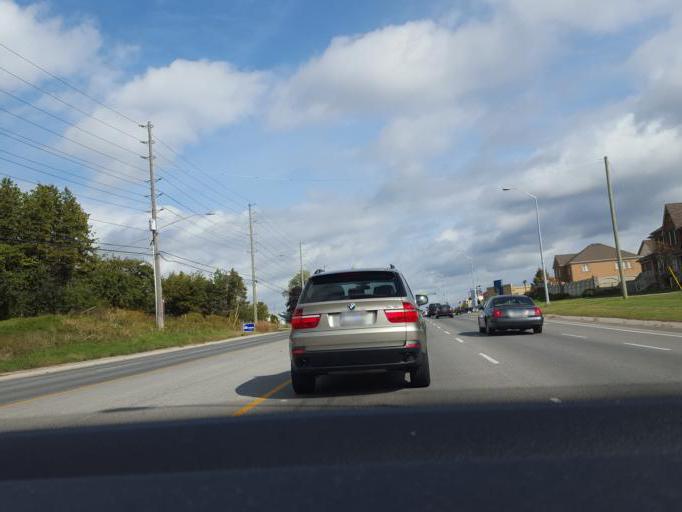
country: CA
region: Ontario
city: Ajax
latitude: 43.8967
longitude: -79.0364
